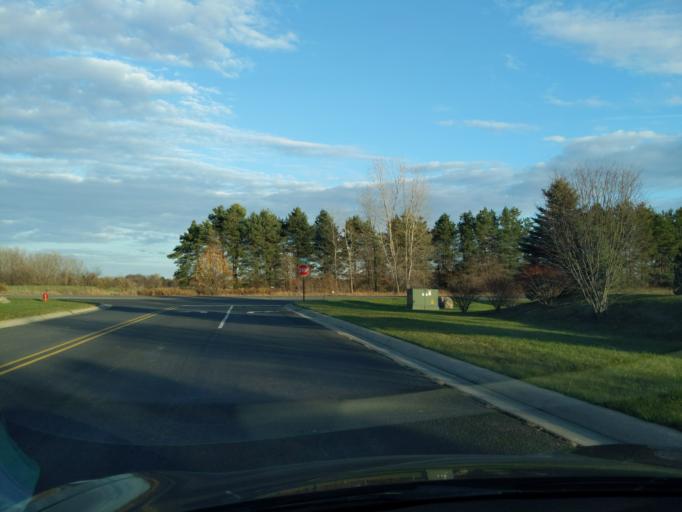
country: US
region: Michigan
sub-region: Ingham County
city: Lansing
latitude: 42.7815
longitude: -84.5237
